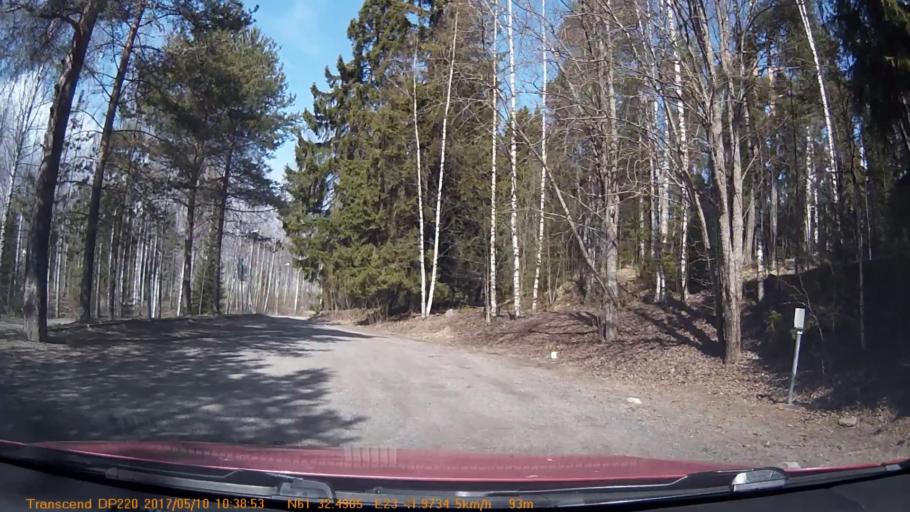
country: FI
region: Pirkanmaa
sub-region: Tampere
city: Tampere
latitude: 61.5416
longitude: 23.6995
